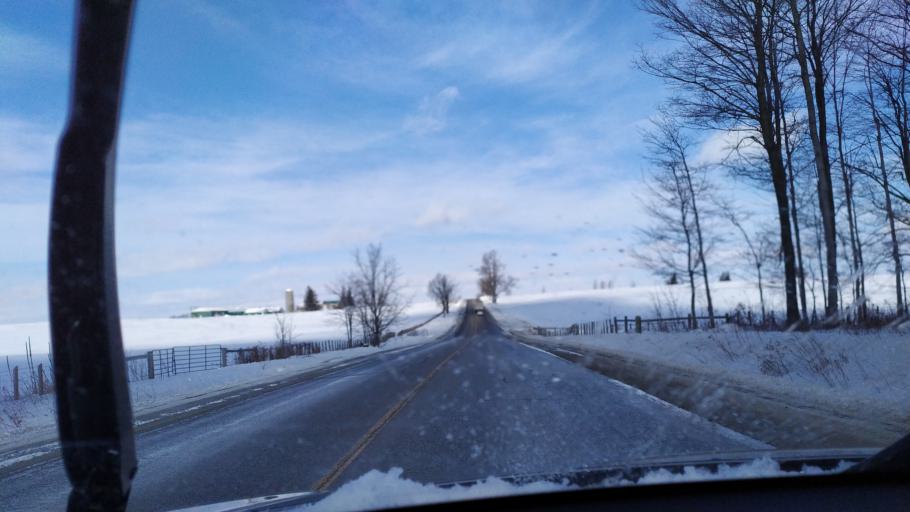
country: CA
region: Ontario
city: Waterloo
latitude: 43.5178
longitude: -80.6836
